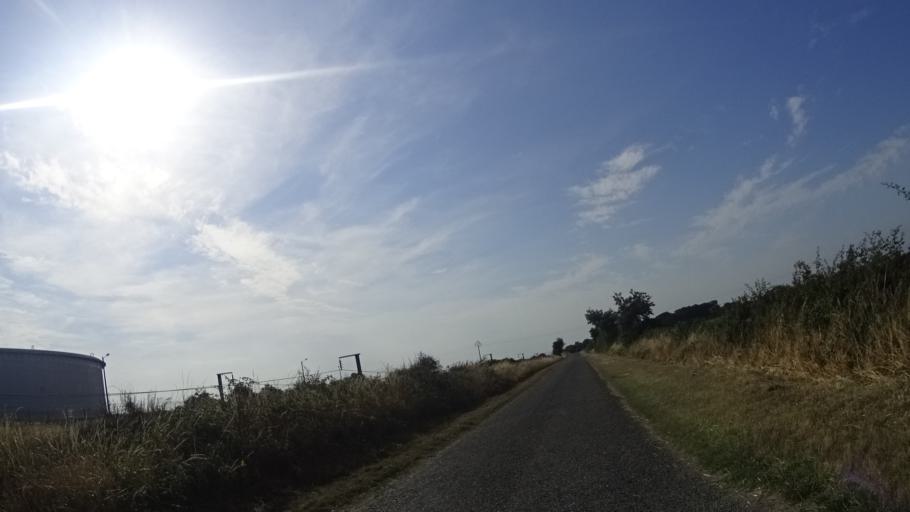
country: FR
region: Pays de la Loire
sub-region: Departement de la Loire-Atlantique
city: Donges
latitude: 47.3196
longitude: -2.0967
